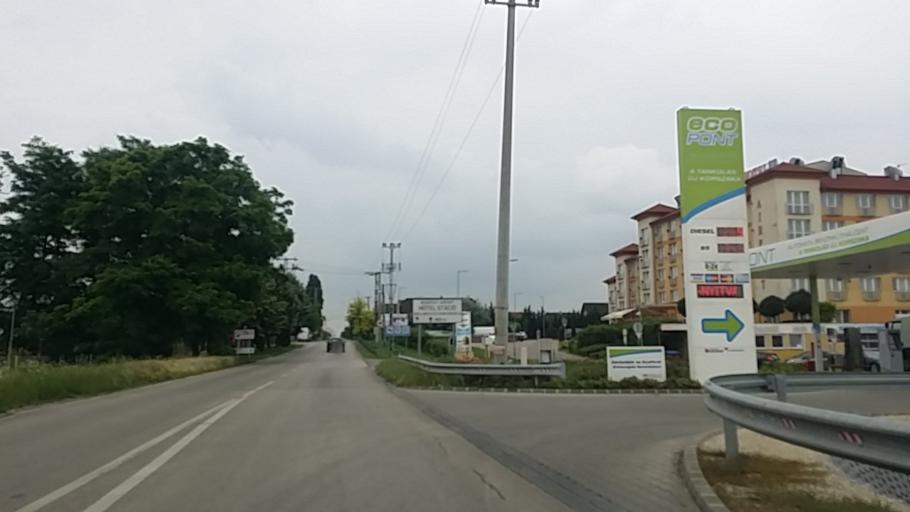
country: HU
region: Pest
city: Gyal
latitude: 47.4152
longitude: 19.2435
